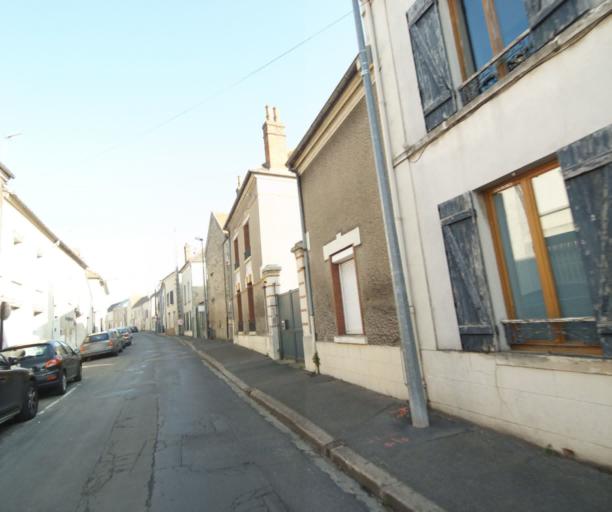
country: FR
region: Ile-de-France
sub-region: Departement du Val-d'Oise
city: Cergy
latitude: 49.0391
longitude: 2.0609
